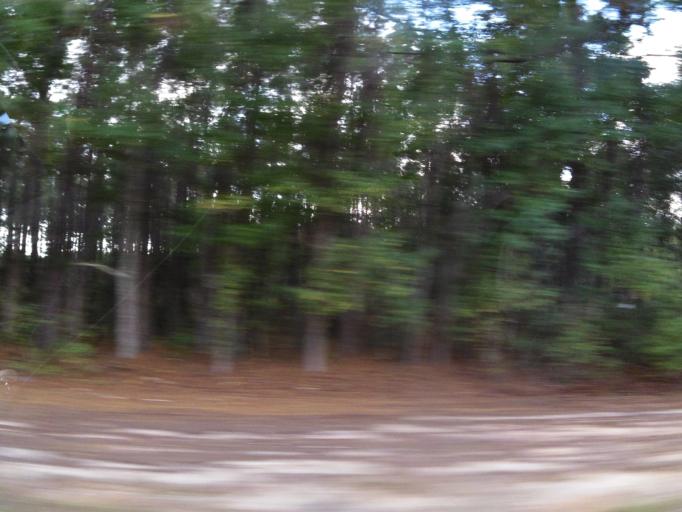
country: US
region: Georgia
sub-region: Liberty County
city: Midway
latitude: 31.6779
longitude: -81.4042
